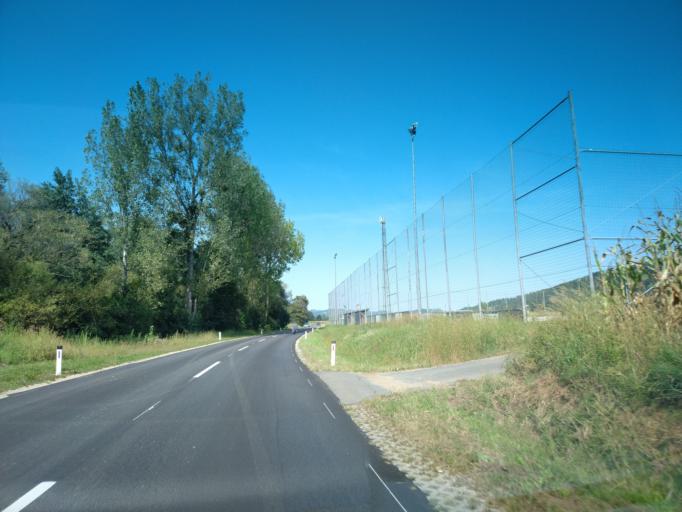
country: AT
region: Styria
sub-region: Politischer Bezirk Leibnitz
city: Sankt Johann im Saggautal
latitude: 46.7033
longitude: 15.3939
